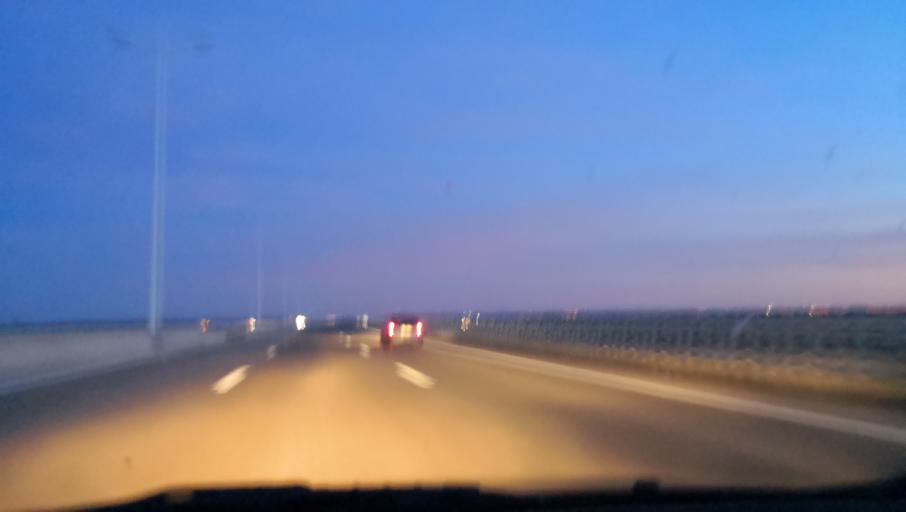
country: PT
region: Lisbon
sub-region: Vila Franca de Xira
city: Castanheira do Ribatejo
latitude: 39.0036
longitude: -8.9097
